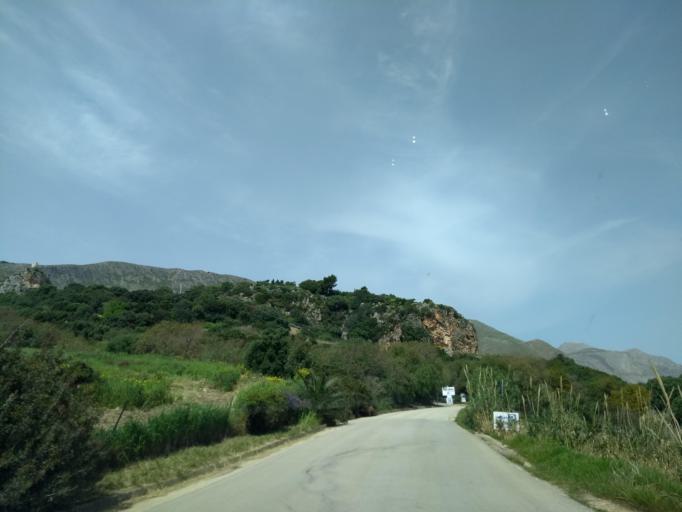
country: IT
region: Sicily
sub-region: Trapani
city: Castellammare del Golfo
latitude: 38.0688
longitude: 12.8220
